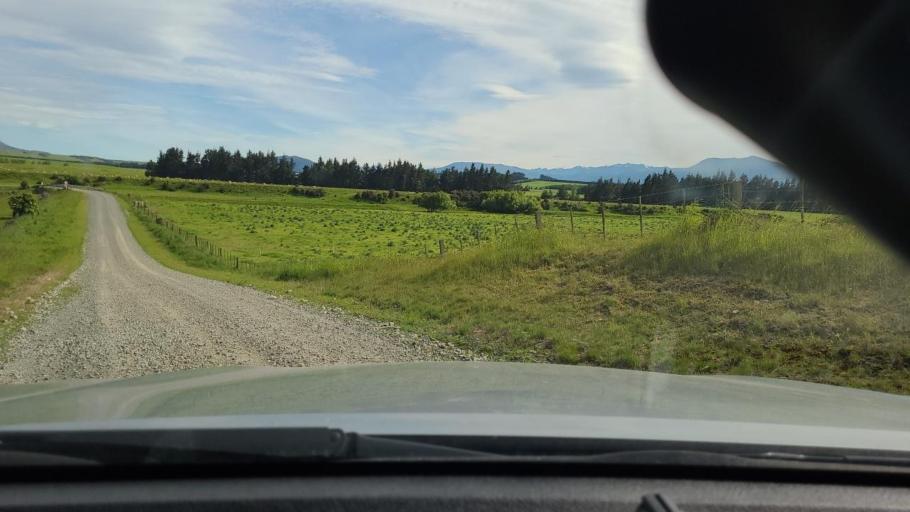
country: NZ
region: Southland
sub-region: Southland District
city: Te Anau
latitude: -45.7024
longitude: 168.0881
